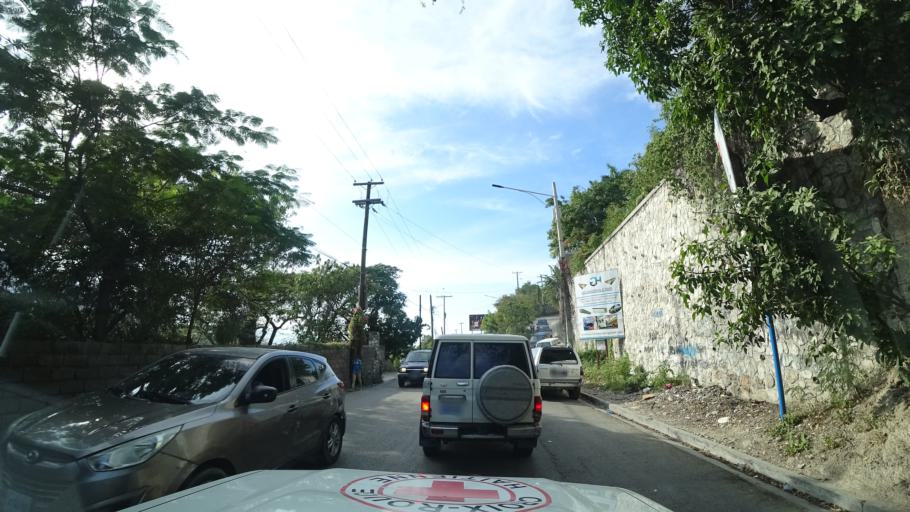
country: HT
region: Ouest
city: Delmas 73
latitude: 18.5337
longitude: -72.3076
